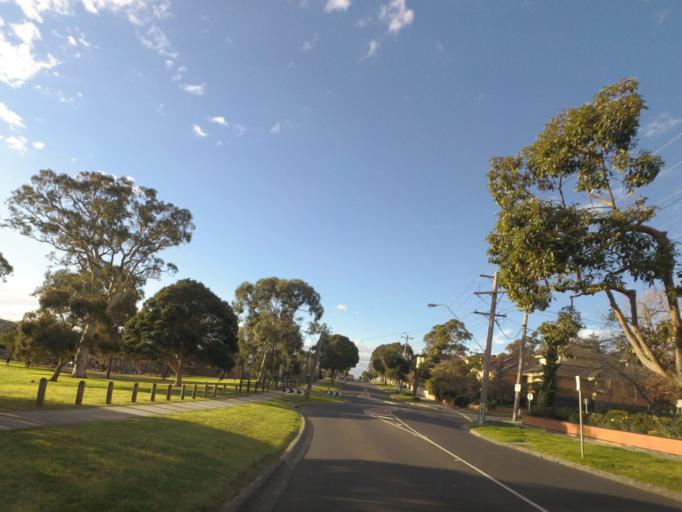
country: AU
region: Victoria
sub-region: Boroondara
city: Balwyn North
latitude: -37.7907
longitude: 145.0856
